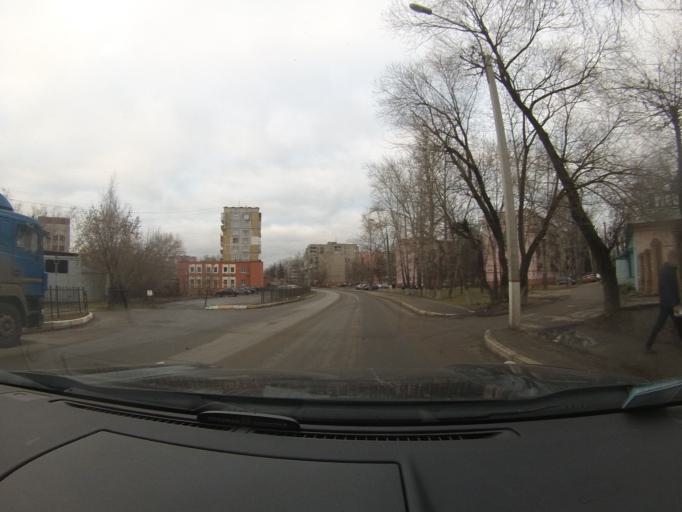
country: RU
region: Moskovskaya
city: Voskresensk
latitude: 55.3185
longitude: 38.6851
